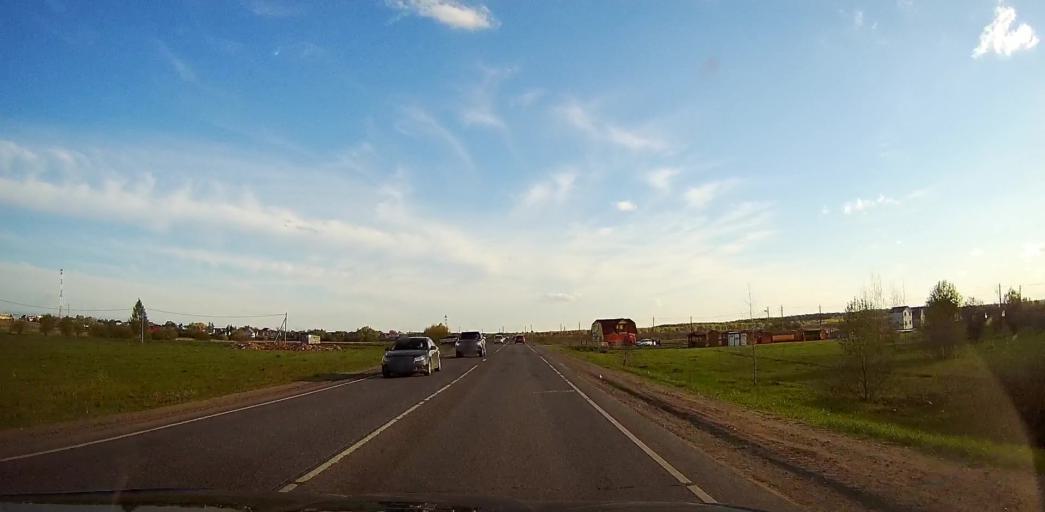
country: RU
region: Moskovskaya
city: Bronnitsy
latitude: 55.3357
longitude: 38.2209
